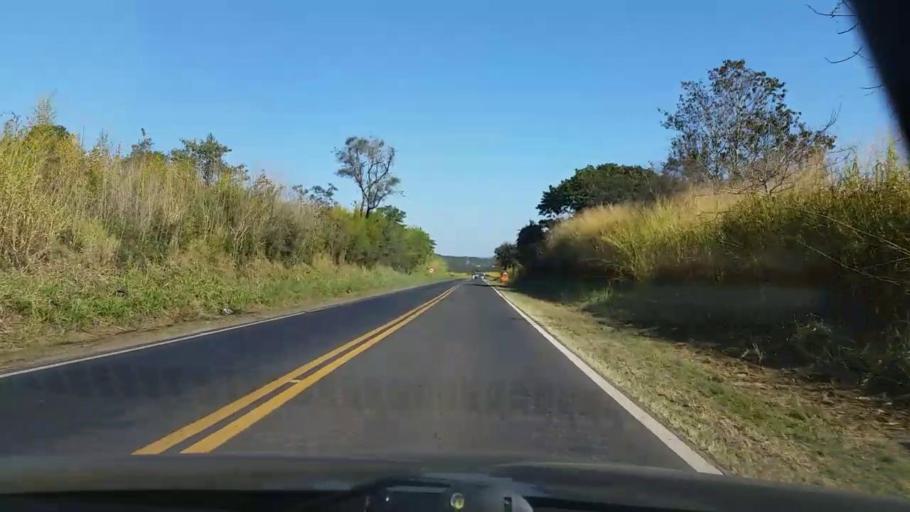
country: BR
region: Sao Paulo
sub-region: Itatinga
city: Itatinga
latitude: -22.9023
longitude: -48.7666
